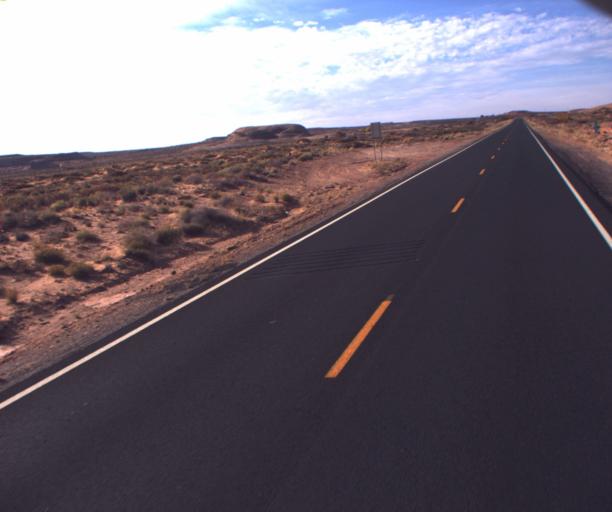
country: US
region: Arizona
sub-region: Apache County
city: Many Farms
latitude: 36.9216
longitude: -109.6174
